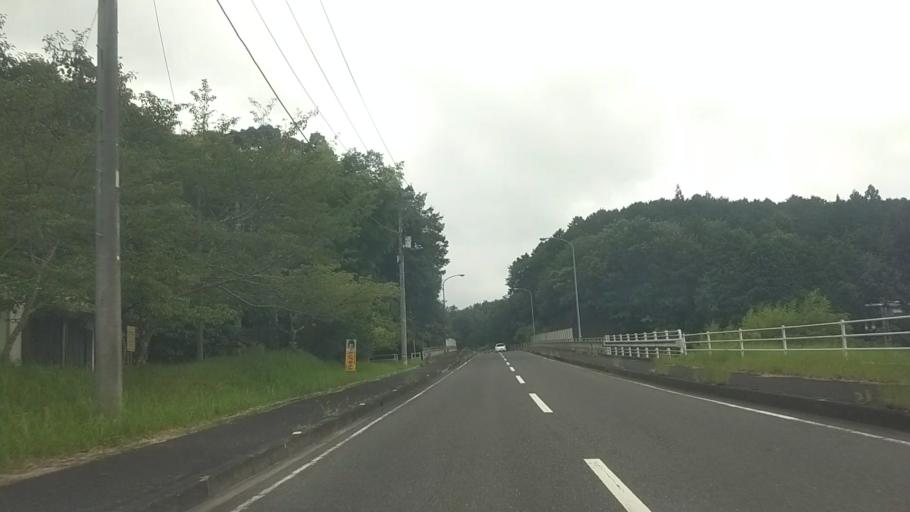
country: JP
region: Chiba
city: Kawaguchi
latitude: 35.2373
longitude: 140.0857
